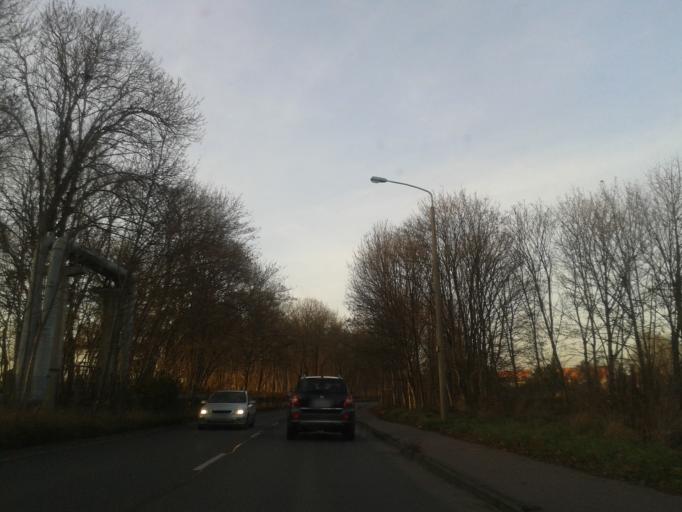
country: DE
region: Saxony
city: Dresden
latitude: 51.0184
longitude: 13.8068
